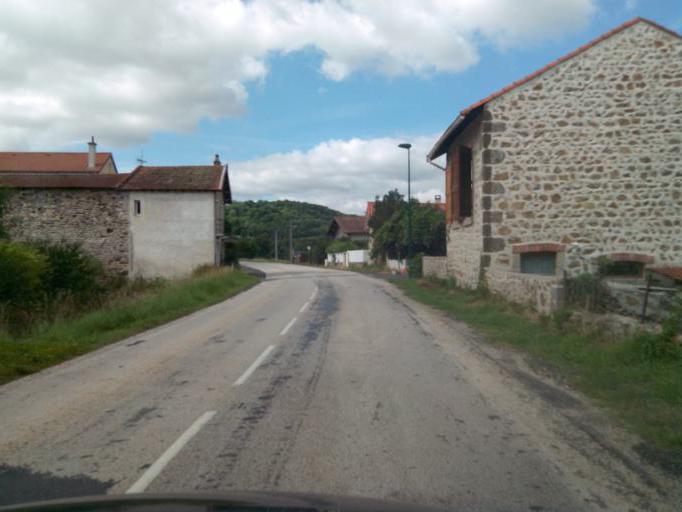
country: FR
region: Auvergne
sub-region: Departement de la Haute-Loire
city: Chadrac
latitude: 45.0742
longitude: 3.9052
